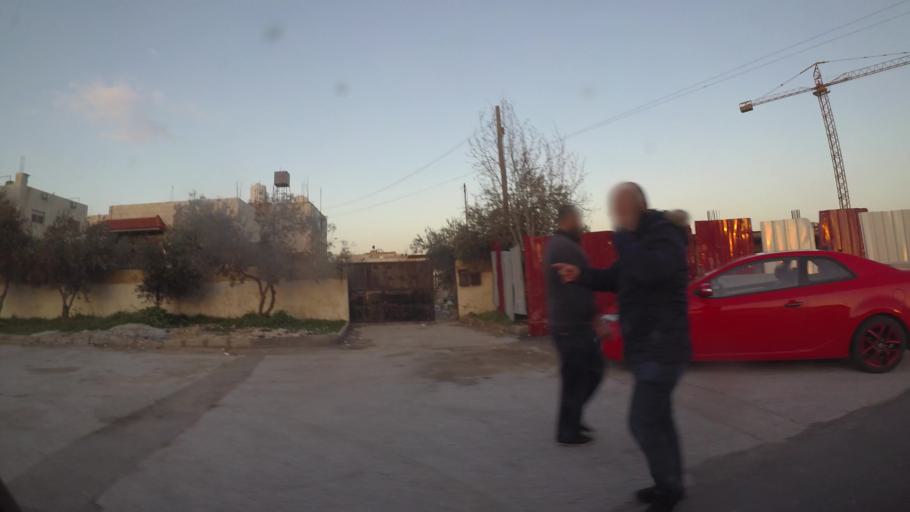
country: JO
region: Amman
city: Al Jubayhah
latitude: 31.9978
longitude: 35.8531
